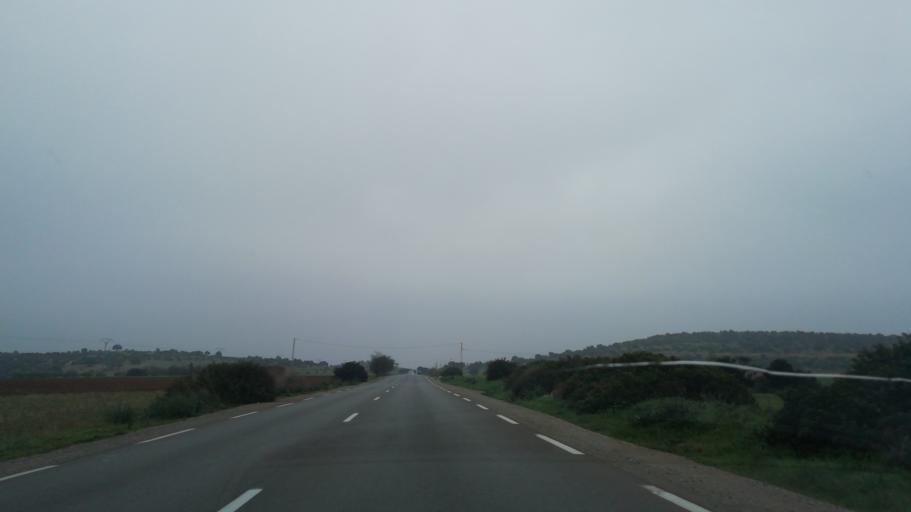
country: DZ
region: Mascara
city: Oued el Abtal
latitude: 35.2968
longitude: 0.4542
